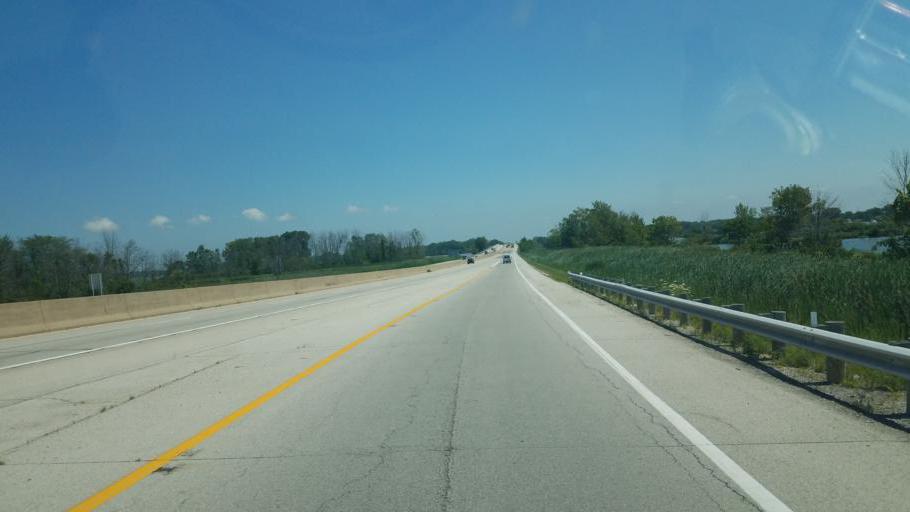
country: US
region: Ohio
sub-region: Ottawa County
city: Port Clinton
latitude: 41.5174
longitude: -82.9992
